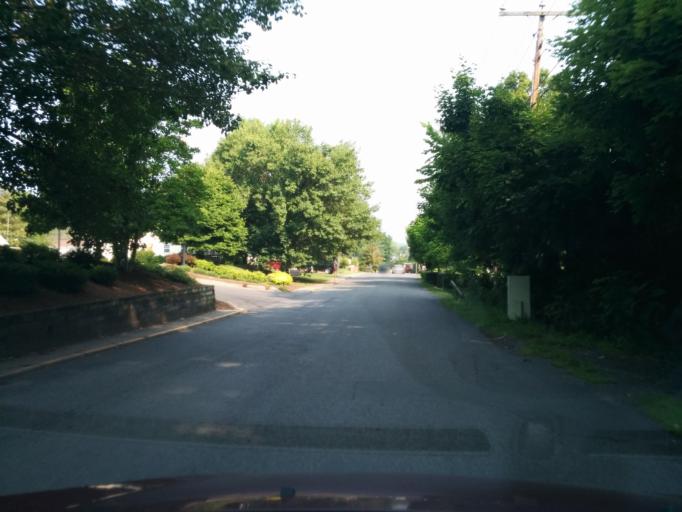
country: US
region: Virginia
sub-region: City of Lexington
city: Lexington
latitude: 37.7755
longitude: -79.4416
